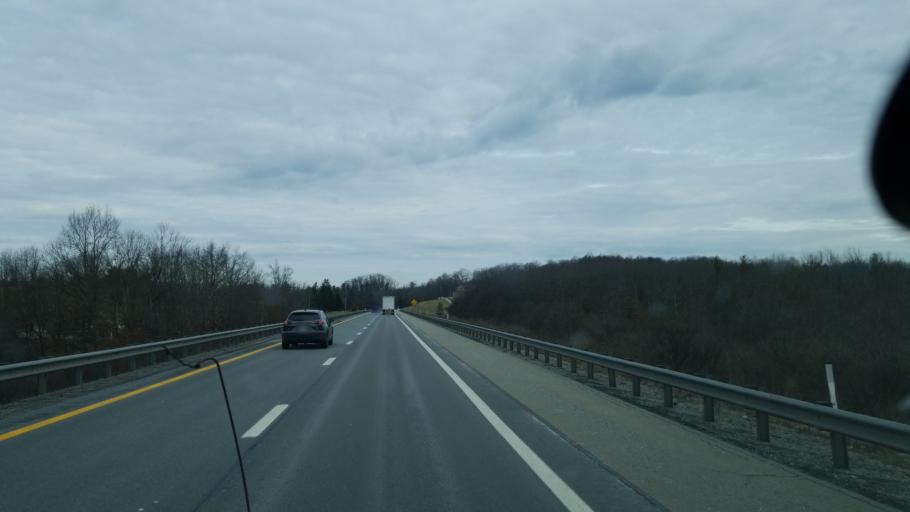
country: US
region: West Virginia
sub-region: Raleigh County
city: Shady Spring
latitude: 37.6471
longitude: -81.1088
